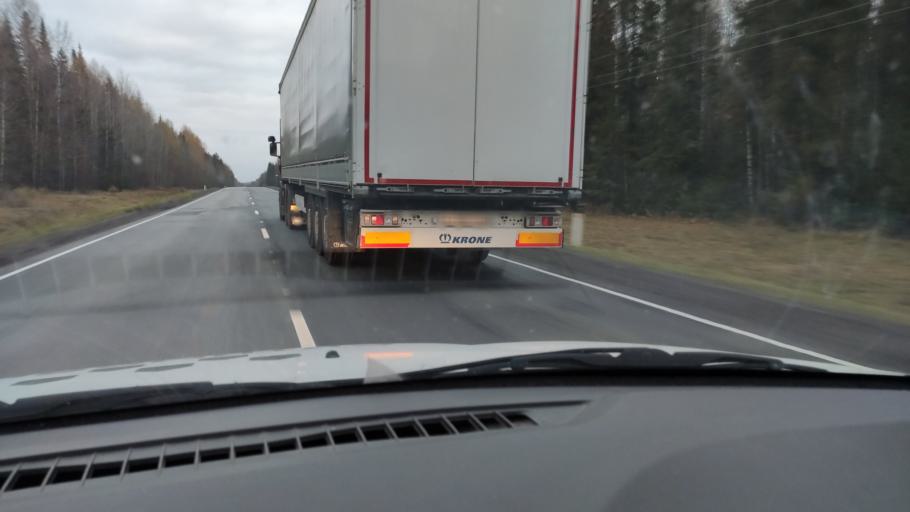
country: RU
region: Kirov
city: Belorechensk
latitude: 58.8027
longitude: 52.4245
